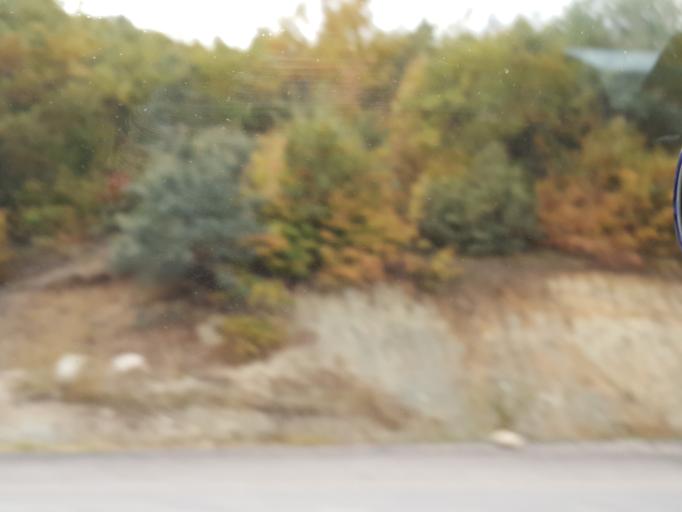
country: TR
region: Amasya
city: Gediksaray
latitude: 40.4618
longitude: 35.7805
